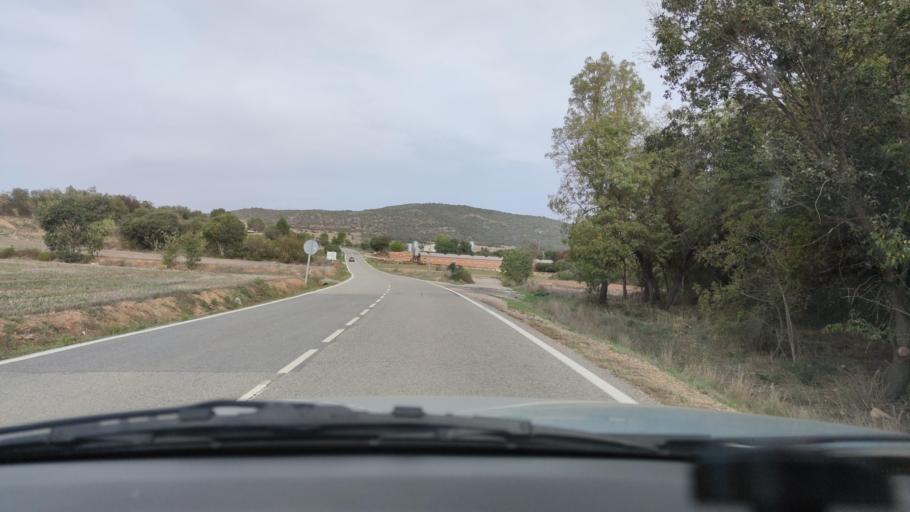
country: ES
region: Catalonia
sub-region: Provincia de Lleida
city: Artesa de Segre
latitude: 41.9202
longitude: 1.0736
